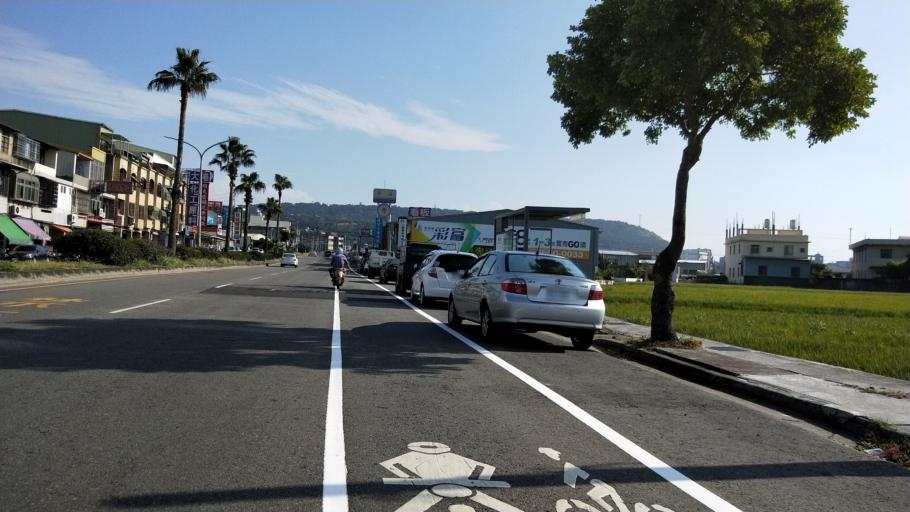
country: TW
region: Taiwan
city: Fengyuan
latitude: 24.3434
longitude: 120.6174
